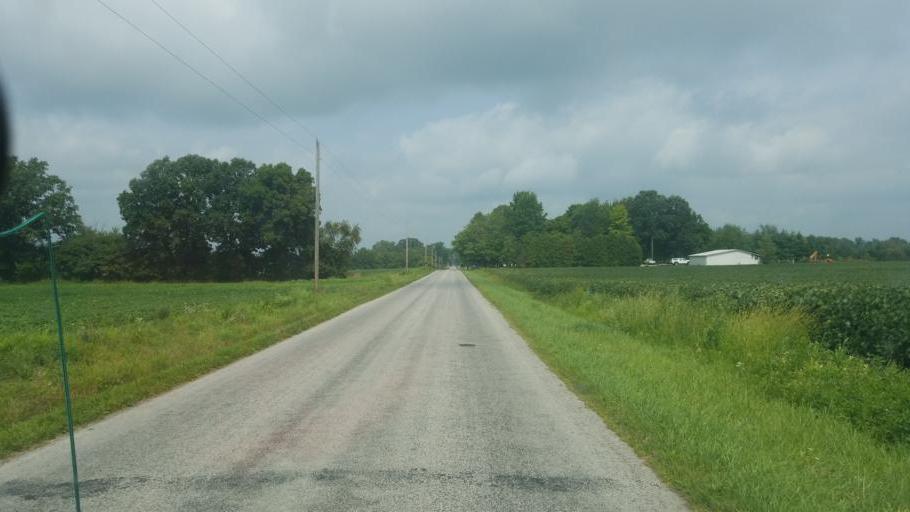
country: US
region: Ohio
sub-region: Huron County
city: Greenwich
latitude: 41.0151
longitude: -82.5101
